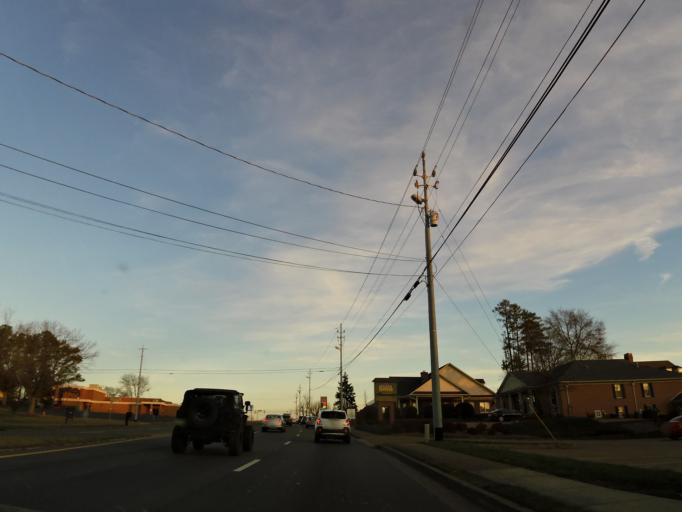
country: US
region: Tennessee
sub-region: Bradley County
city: Cleveland
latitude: 35.1801
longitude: -84.8695
